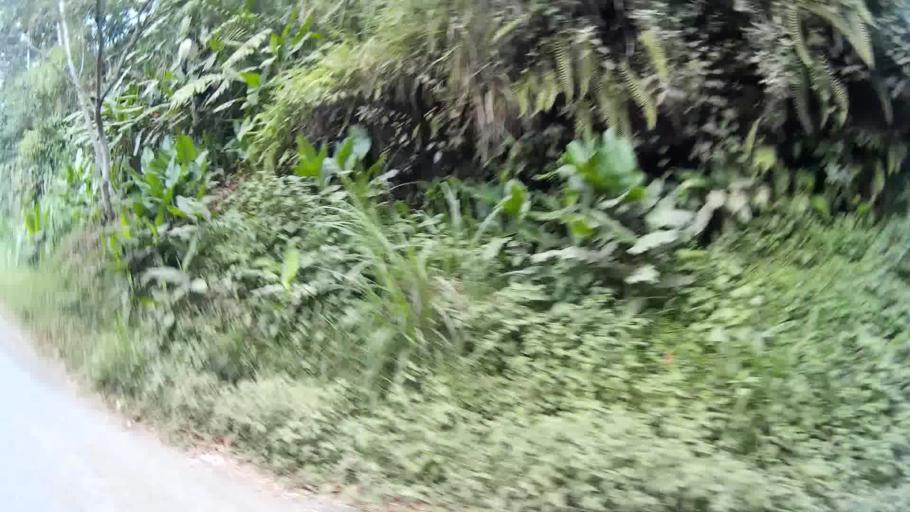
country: CO
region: Risaralda
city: Pereira
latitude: 4.8473
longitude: -75.7618
